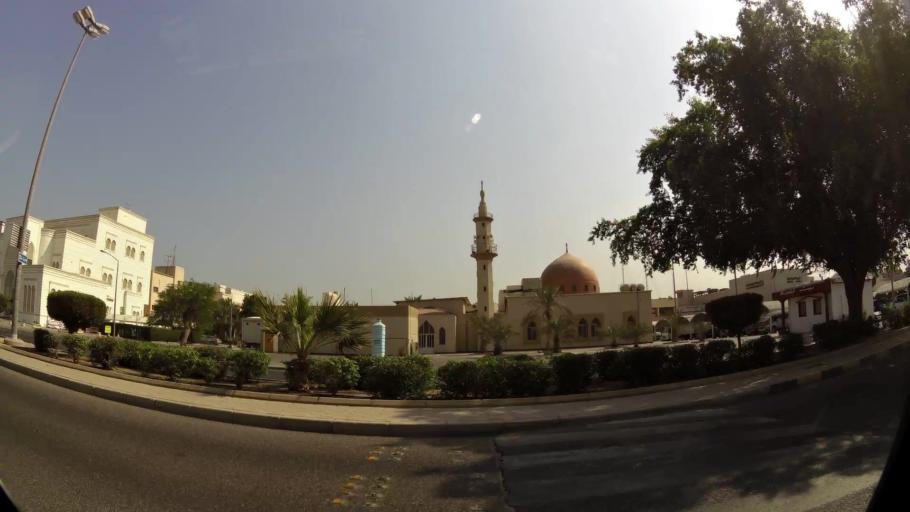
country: KW
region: Muhafazat Hawalli
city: Hawalli
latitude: 29.3522
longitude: 48.0213
